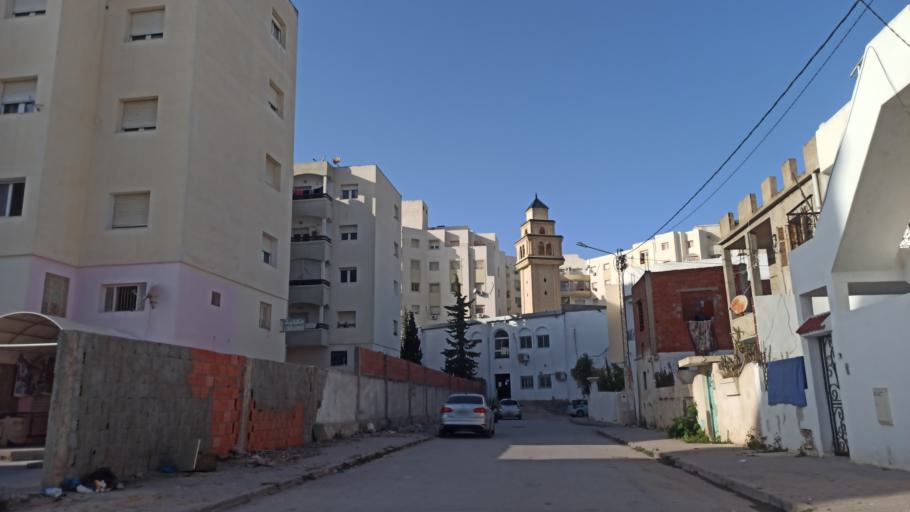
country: TN
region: Tunis
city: La Goulette
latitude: 36.8557
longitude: 10.2698
